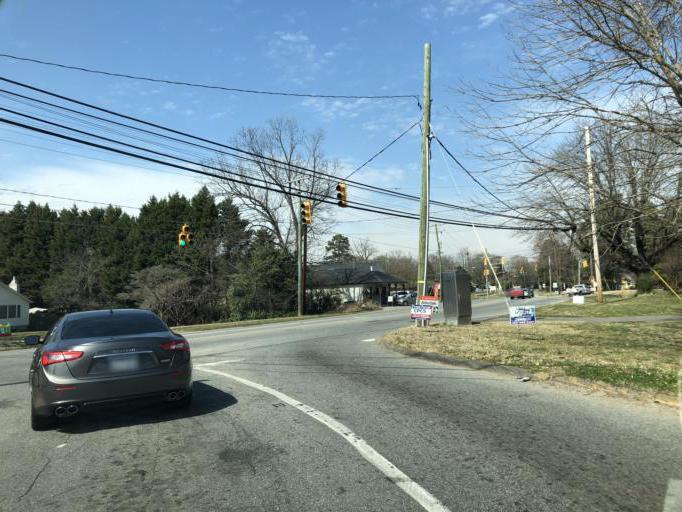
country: US
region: North Carolina
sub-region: Gaston County
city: Stanley
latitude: 35.3491
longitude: -81.0940
